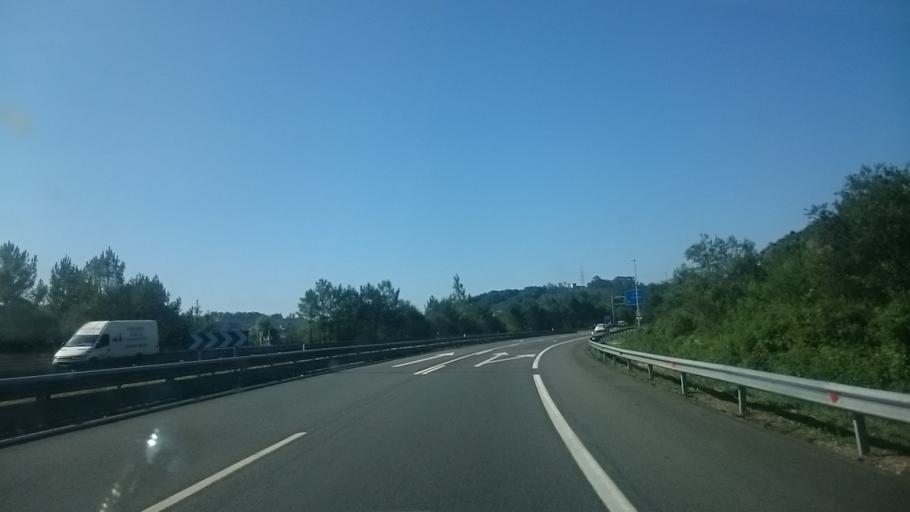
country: ES
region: Asturias
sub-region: Province of Asturias
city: Castandiello
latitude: 43.3117
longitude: -5.8679
